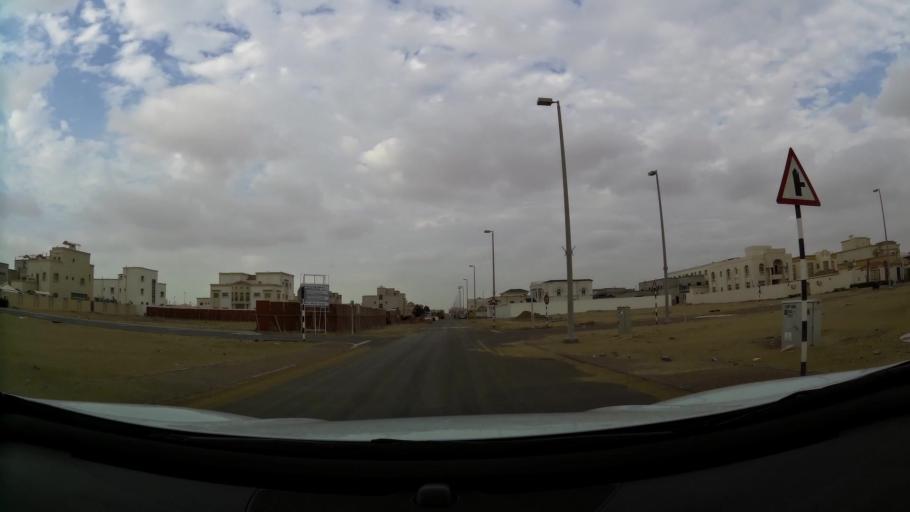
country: AE
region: Abu Dhabi
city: Abu Dhabi
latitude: 24.3482
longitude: 54.6079
